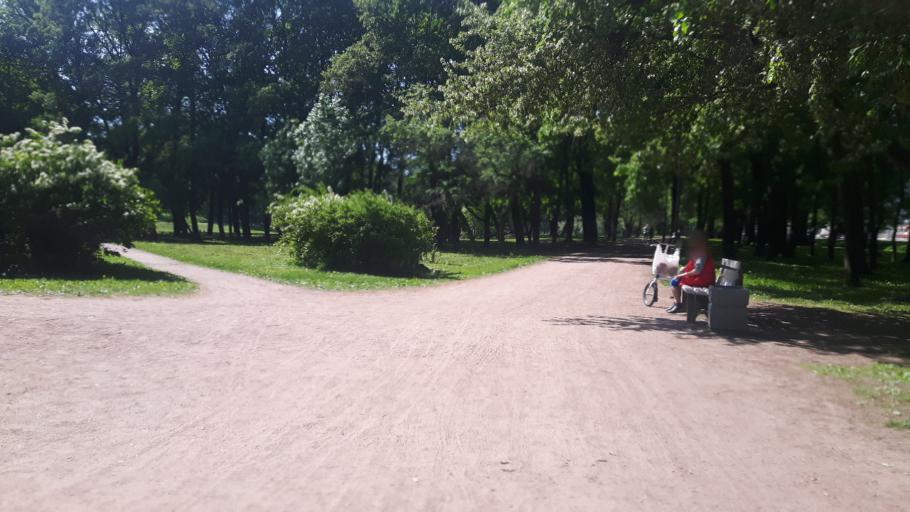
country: RU
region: St.-Petersburg
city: Sosnovaya Polyana
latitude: 59.8467
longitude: 30.1393
